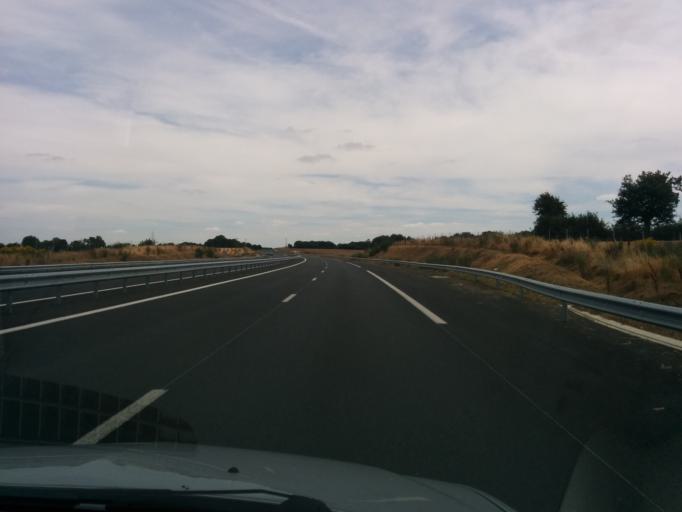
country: FR
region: Poitou-Charentes
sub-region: Departement des Deux-Sevres
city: Nueil-les-Aubiers
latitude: 46.8820
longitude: -0.5988
